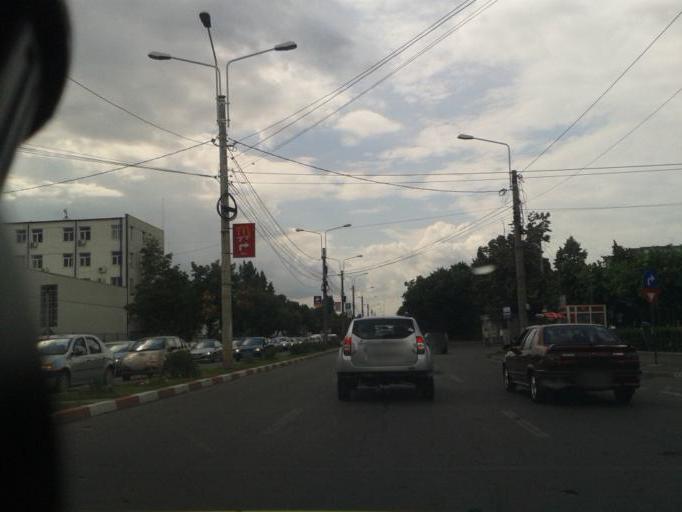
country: RO
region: Prahova
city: Ploiesti
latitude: 44.9518
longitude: 26.0000
